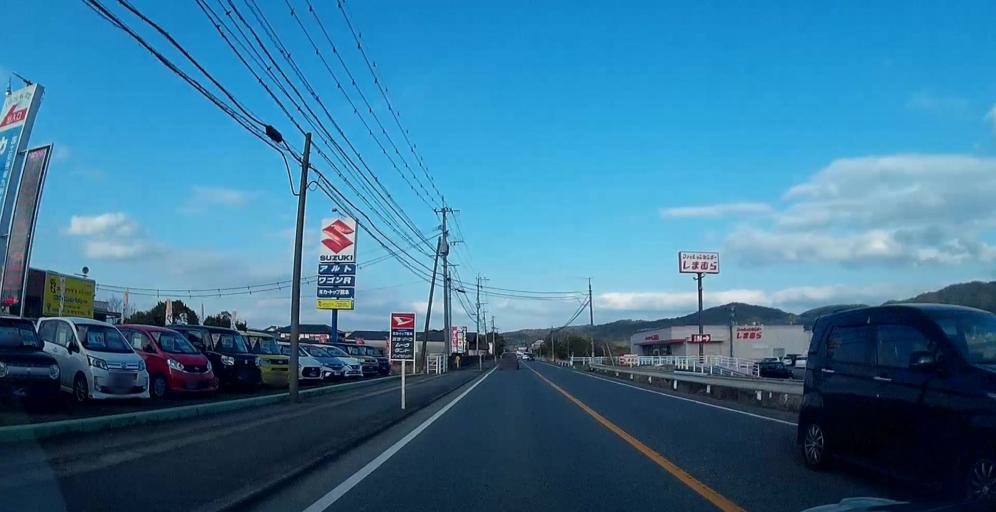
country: JP
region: Kumamoto
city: Matsubase
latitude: 32.6061
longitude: 130.7036
